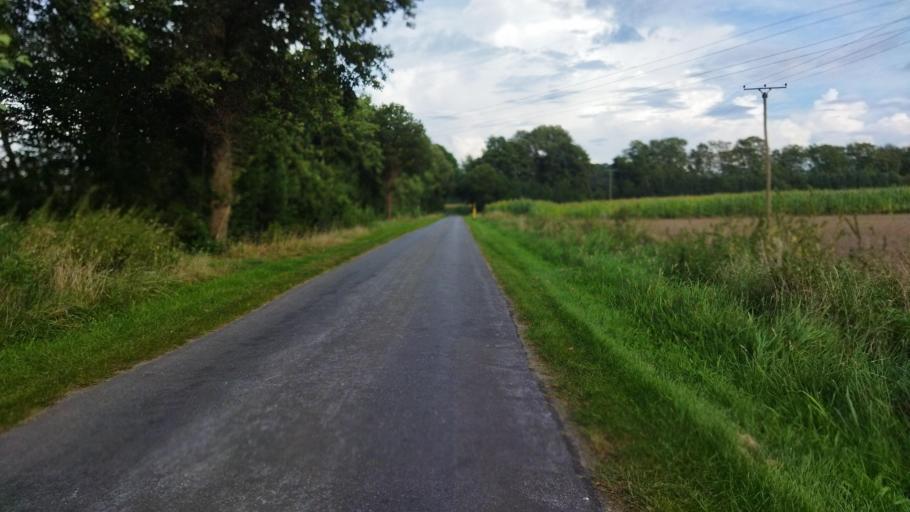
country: DE
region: North Rhine-Westphalia
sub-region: Regierungsbezirk Munster
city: Ostbevern
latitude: 52.0307
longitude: 7.8064
